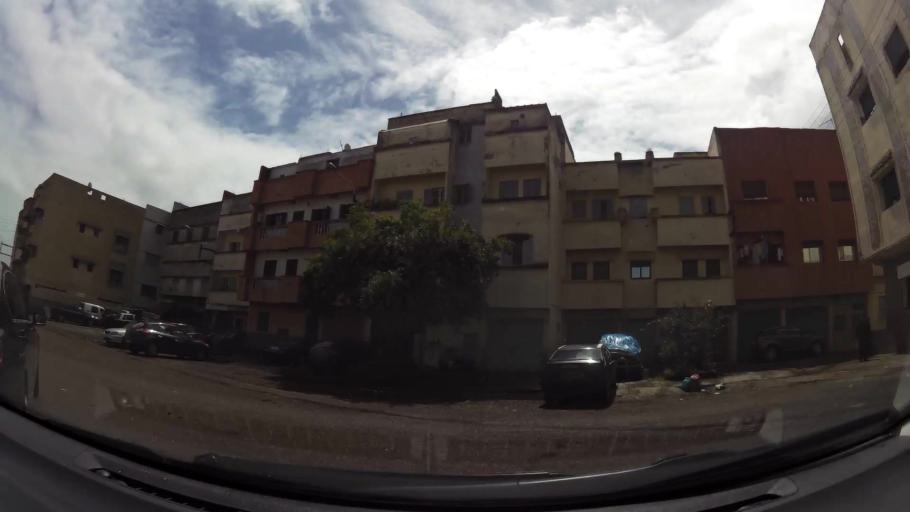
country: MA
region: Grand Casablanca
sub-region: Casablanca
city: Casablanca
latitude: 33.5529
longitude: -7.6750
